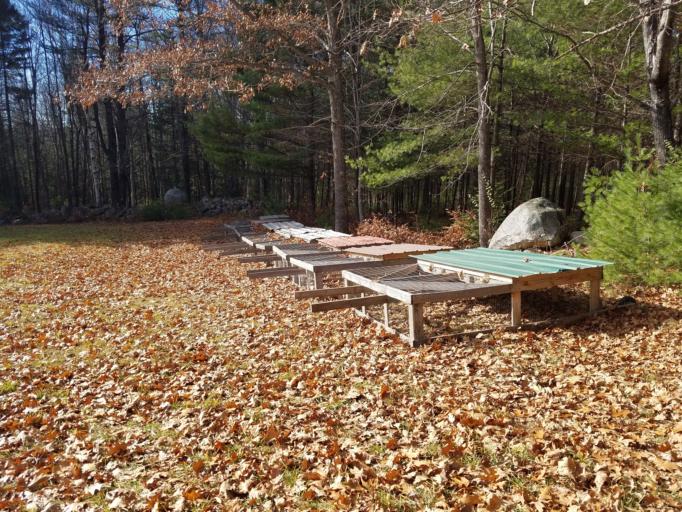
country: US
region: New Hampshire
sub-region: Carroll County
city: Ossipee
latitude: 43.6853
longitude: -71.0550
